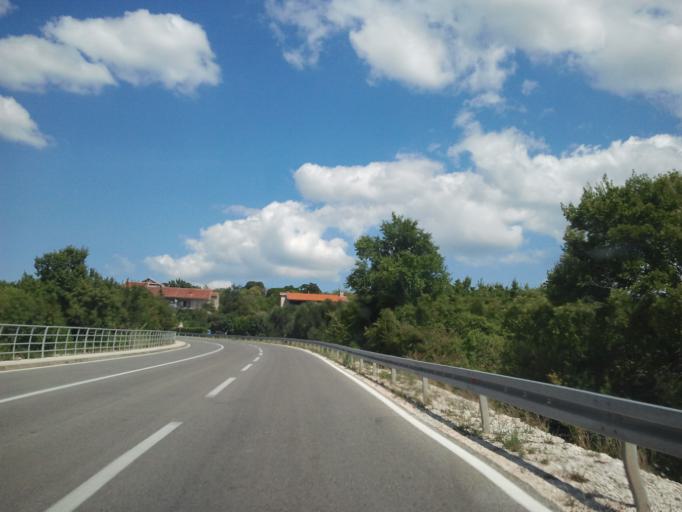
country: HR
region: Zadarska
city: Benkovac
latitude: 44.0359
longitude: 15.6192
